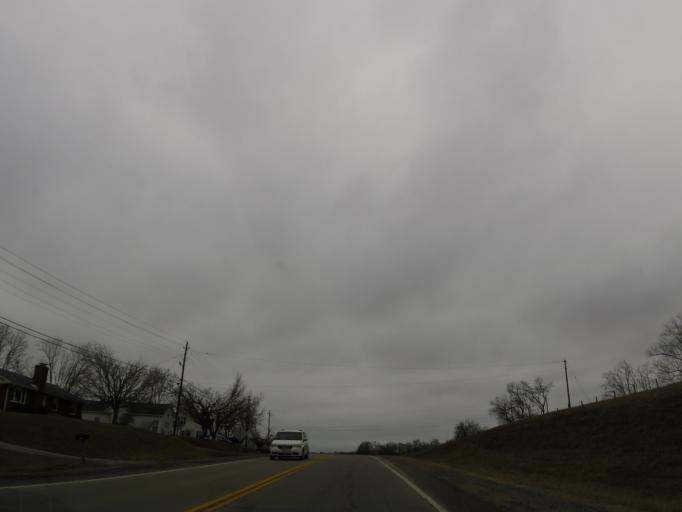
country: US
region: Kentucky
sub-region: Henry County
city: New Castle
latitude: 38.4282
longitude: -85.1706
